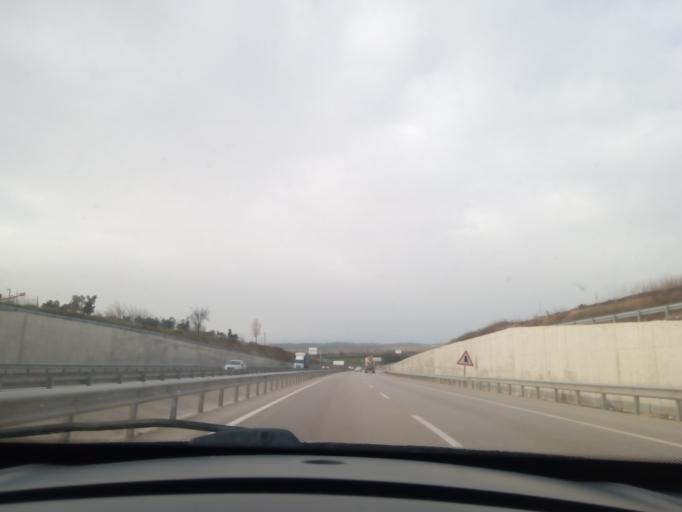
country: TR
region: Bursa
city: Gorukle
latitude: 40.2159
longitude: 28.7511
